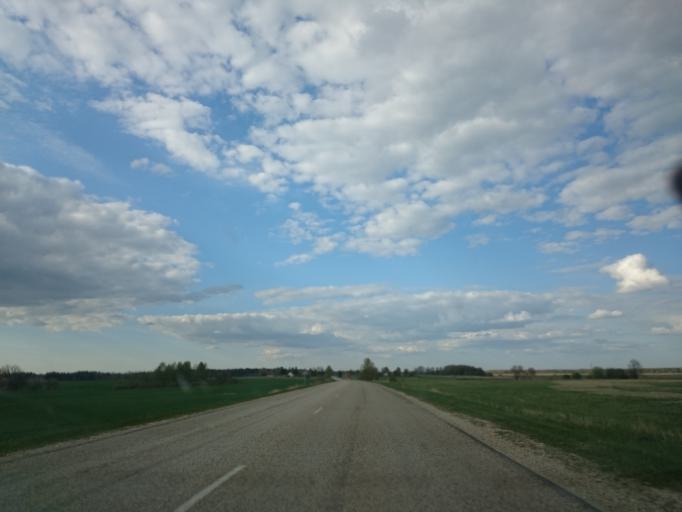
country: LV
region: Aizpute
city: Aizpute
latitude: 56.7530
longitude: 21.6143
